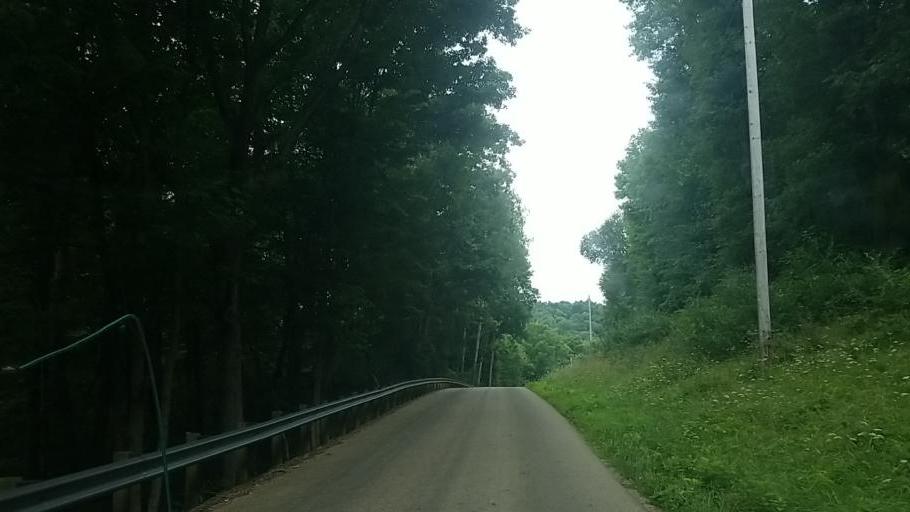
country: US
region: Ohio
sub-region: Licking County
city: Utica
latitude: 40.2460
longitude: -82.2890
